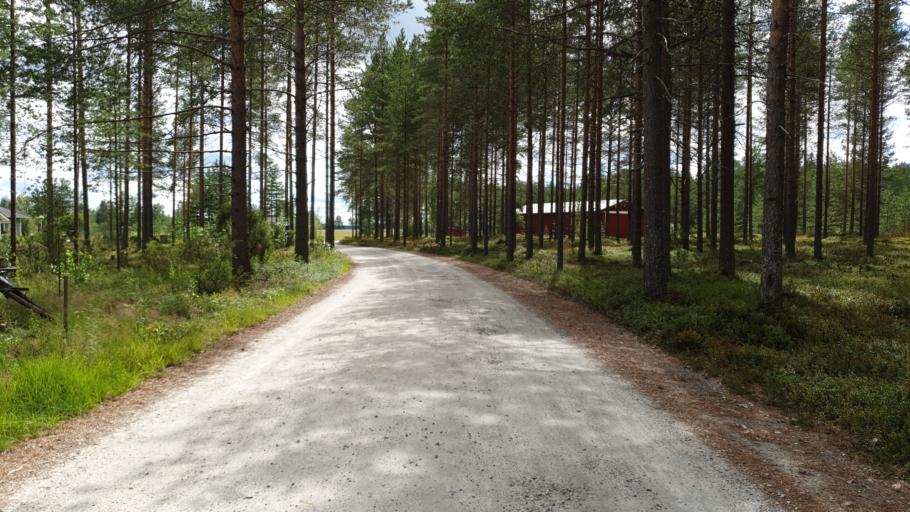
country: FI
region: Kainuu
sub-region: Kehys-Kainuu
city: Kuhmo
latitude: 64.3840
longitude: 29.8084
